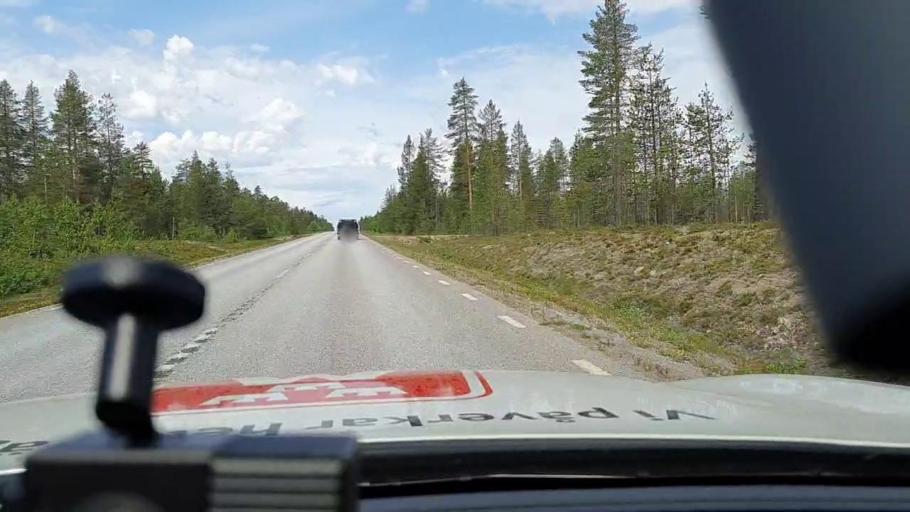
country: SE
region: Norrbotten
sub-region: Jokkmokks Kommun
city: Jokkmokk
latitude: 66.5241
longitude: 20.2020
